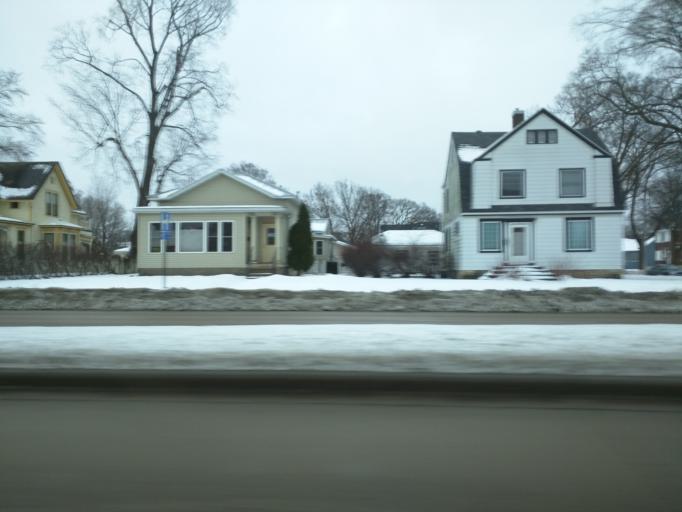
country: US
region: Wisconsin
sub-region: La Crosse County
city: La Crosse
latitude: 43.8040
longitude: -91.2395
